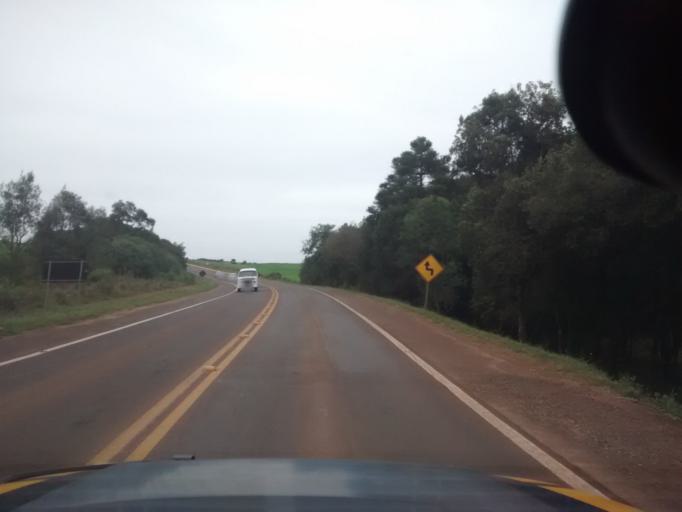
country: BR
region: Rio Grande do Sul
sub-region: Vacaria
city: Vacaria
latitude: -28.4418
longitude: -50.9970
